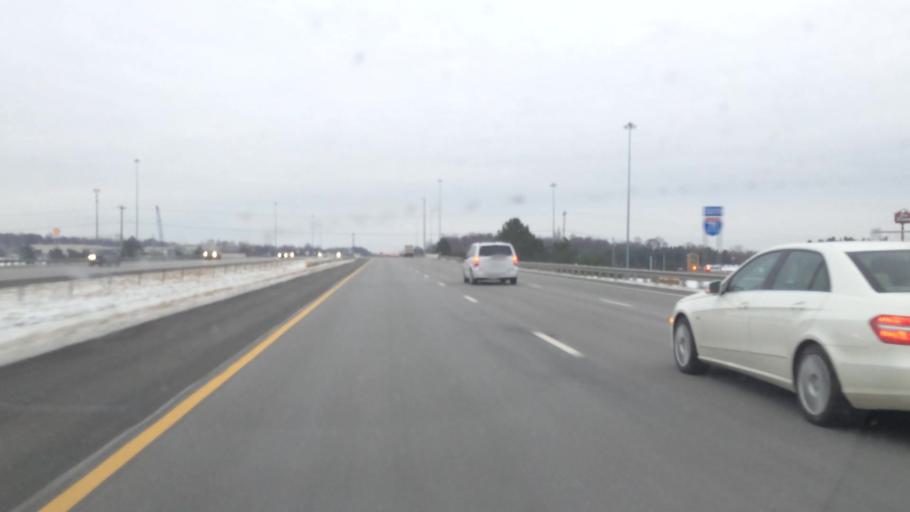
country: US
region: Ohio
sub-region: Medina County
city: Brunswick
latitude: 41.2404
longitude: -81.7991
